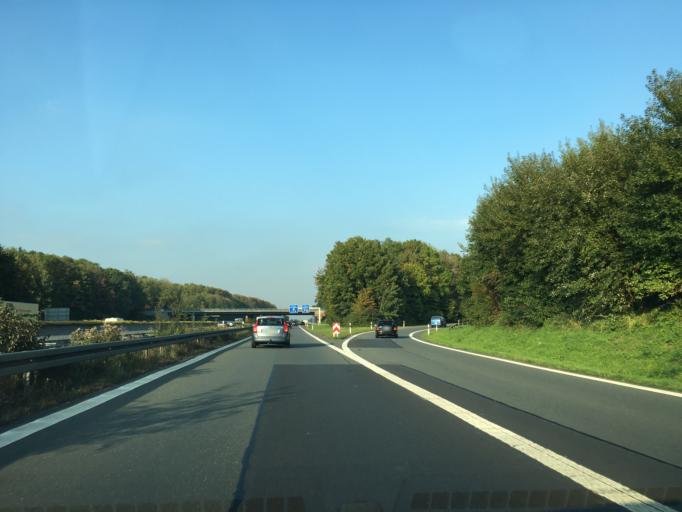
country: DE
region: North Rhine-Westphalia
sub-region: Regierungsbezirk Munster
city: Muenster
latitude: 51.9868
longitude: 7.5576
